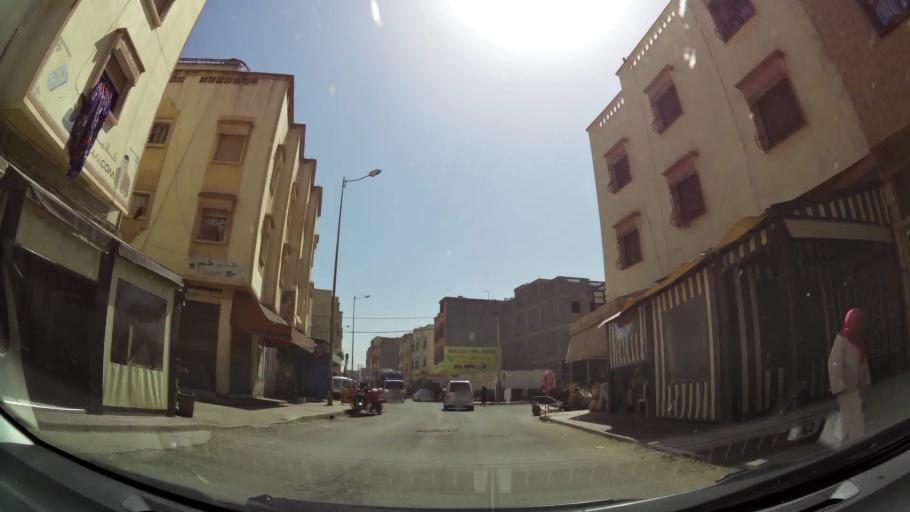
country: MA
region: Souss-Massa-Draa
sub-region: Inezgane-Ait Mellou
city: Inezgane
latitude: 30.3478
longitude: -9.5419
